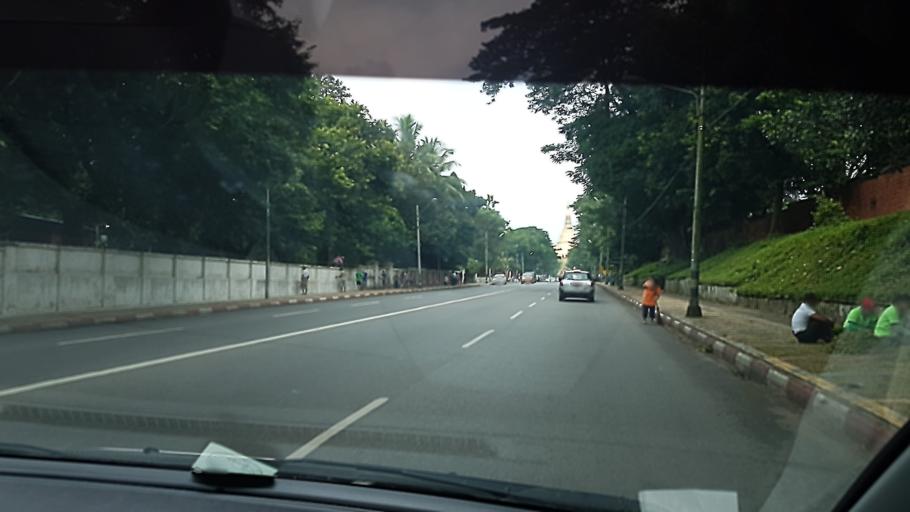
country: MM
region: Yangon
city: Yangon
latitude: 16.7892
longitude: 96.1525
